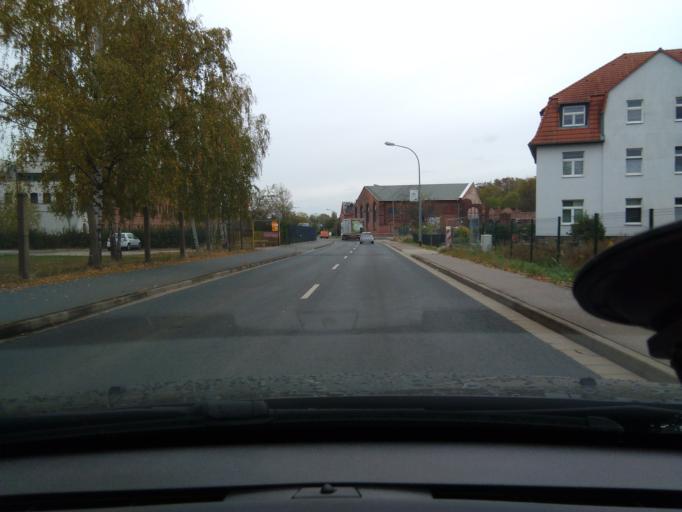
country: DE
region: Saxony
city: Niederau
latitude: 51.1472
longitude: 13.5395
